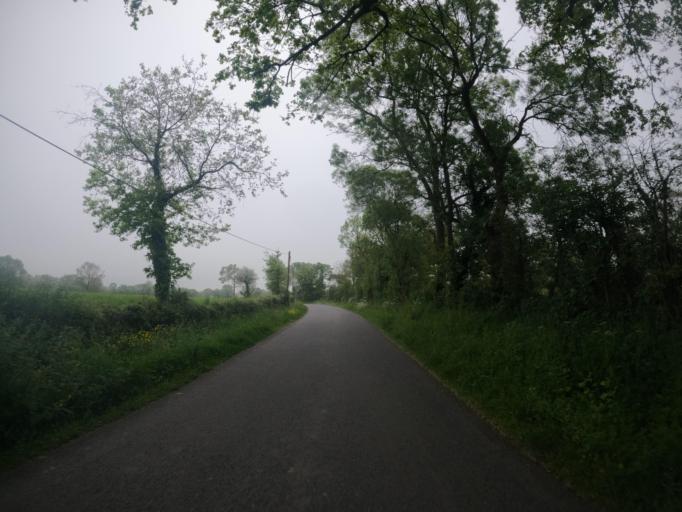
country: FR
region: Poitou-Charentes
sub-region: Departement des Deux-Sevres
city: Chiche
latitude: 46.8712
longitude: -0.3362
